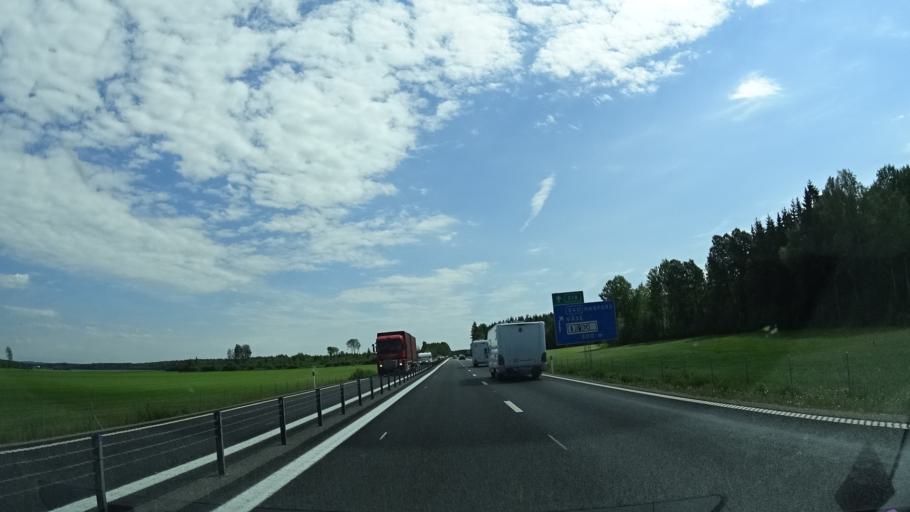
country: SE
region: Vaermland
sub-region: Karlstads Kommun
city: Skattkarr
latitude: 59.3919
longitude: 13.8371
